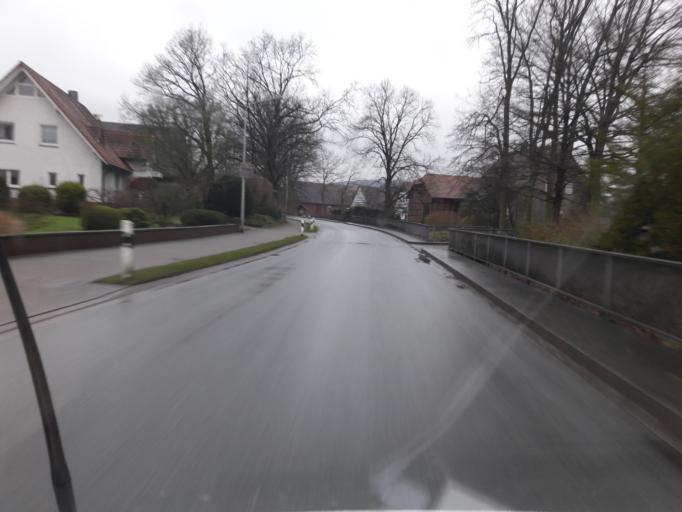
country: DE
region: North Rhine-Westphalia
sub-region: Regierungsbezirk Detmold
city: Hille
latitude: 52.2903
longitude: 8.7977
